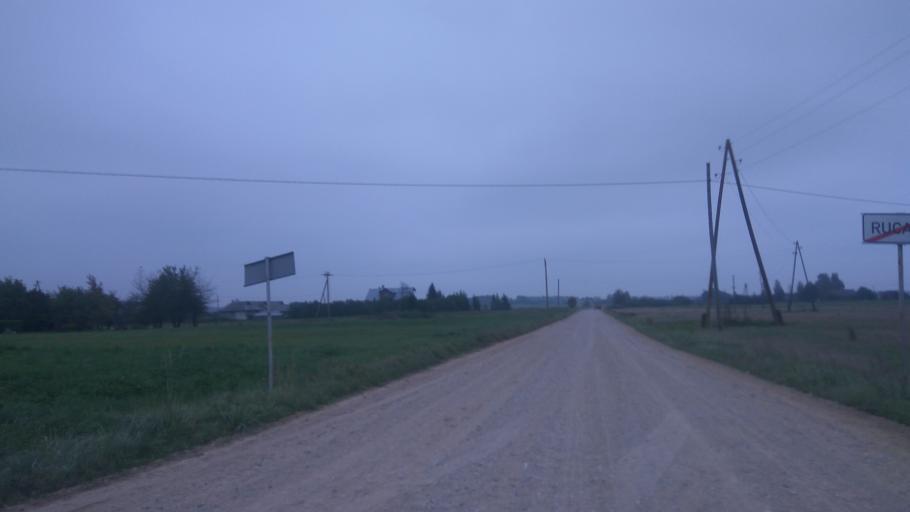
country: LV
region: Rucavas
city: Rucava
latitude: 56.1575
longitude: 21.1696
